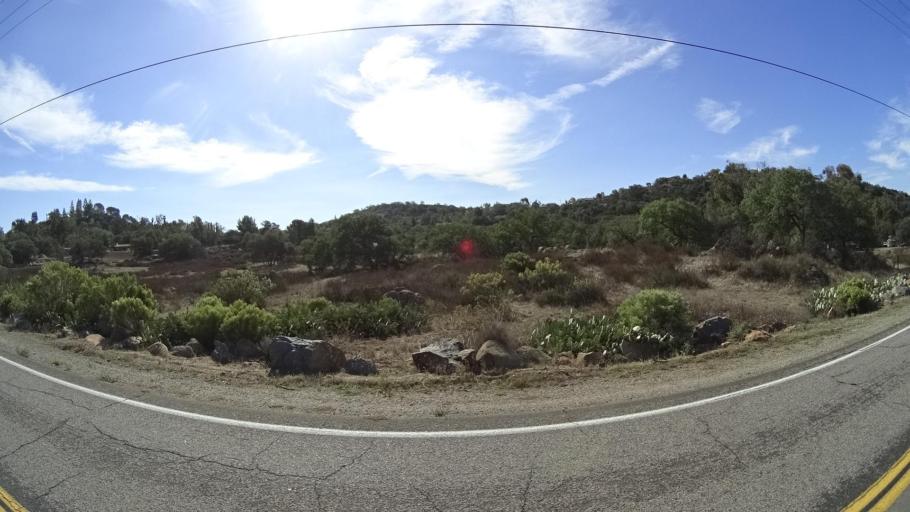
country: US
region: California
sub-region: San Diego County
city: Alpine
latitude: 32.8177
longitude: -116.7612
